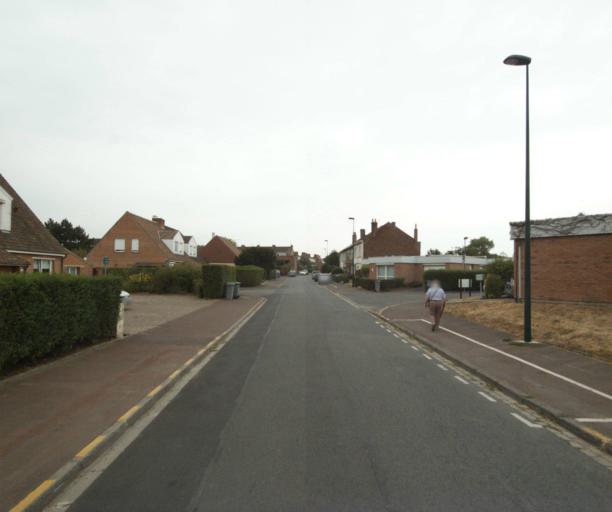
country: FR
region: Nord-Pas-de-Calais
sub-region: Departement du Nord
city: Bondues
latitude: 50.7018
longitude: 3.1019
